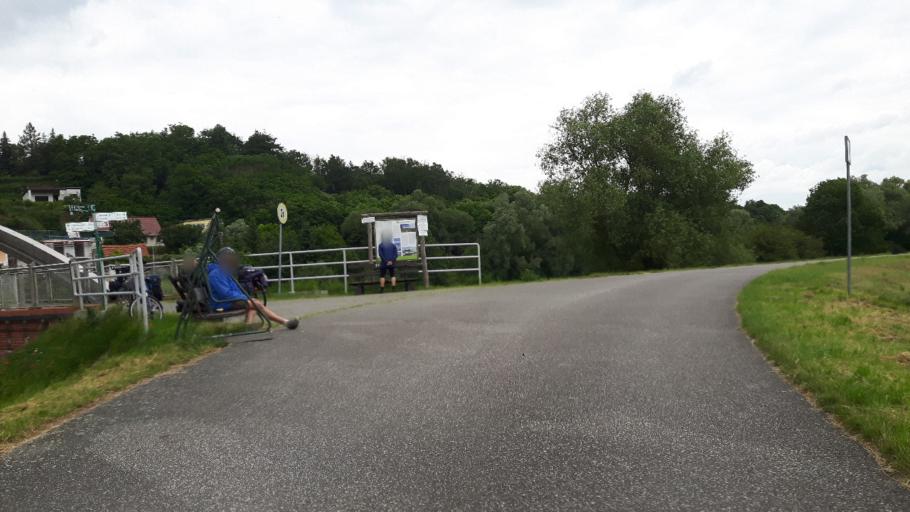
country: DE
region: Brandenburg
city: Schoneberg
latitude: 52.9920
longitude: 14.1759
